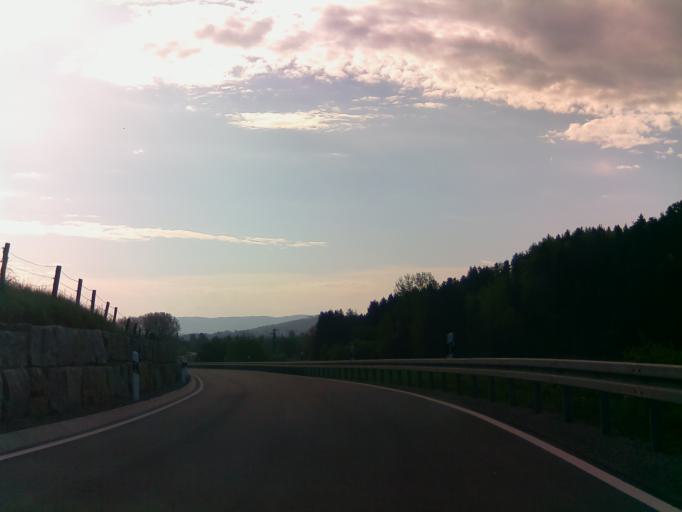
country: DE
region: Baden-Wuerttemberg
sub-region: Karlsruhe Region
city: Empfingen
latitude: 48.3490
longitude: 8.7477
